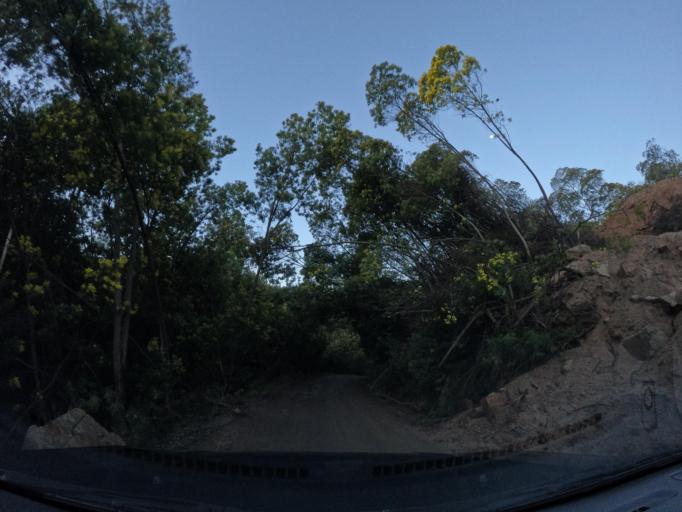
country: CL
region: Biobio
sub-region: Provincia de Concepcion
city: Chiguayante
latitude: -36.9942
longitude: -72.8308
